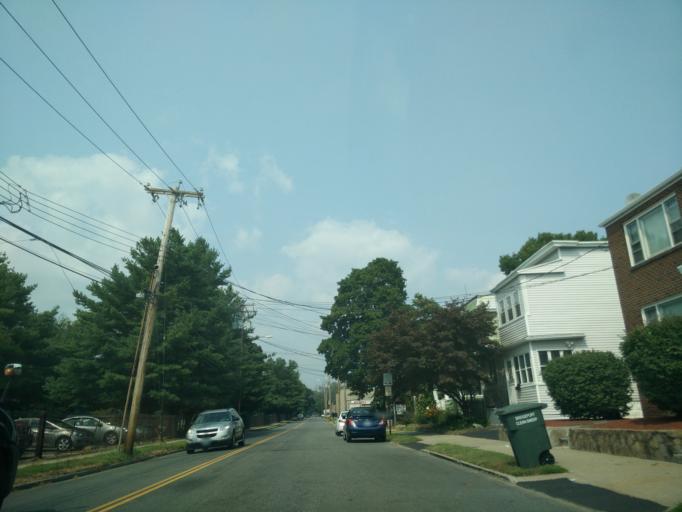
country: US
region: Connecticut
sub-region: Fairfield County
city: Bridgeport
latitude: 41.1700
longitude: -73.2185
